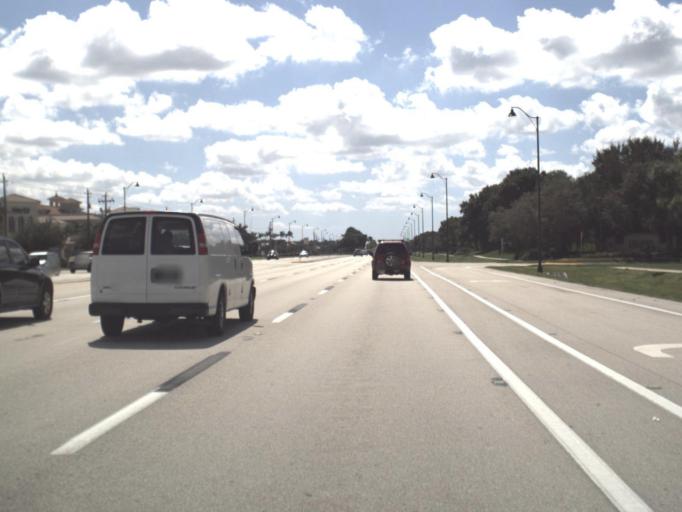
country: US
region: Florida
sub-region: Lee County
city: Bonita Springs
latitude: 26.3598
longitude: -81.8079
